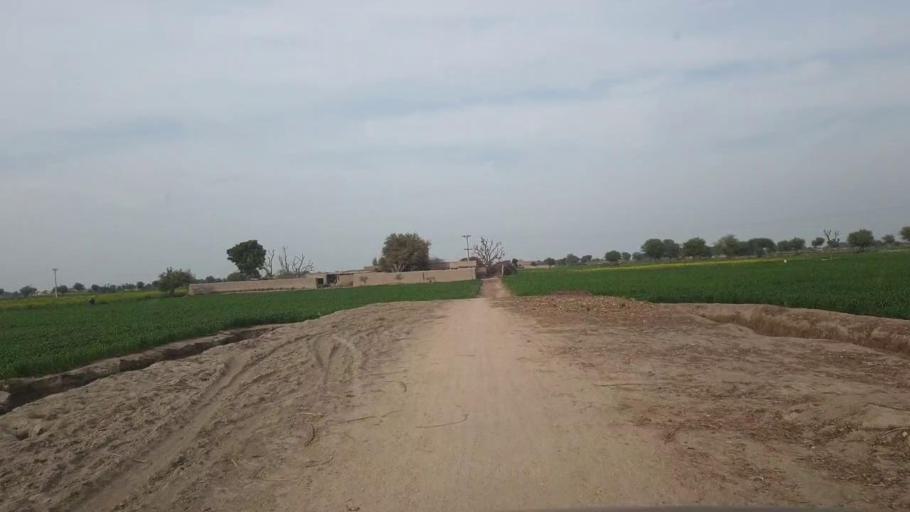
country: PK
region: Sindh
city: Shahpur Chakar
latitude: 26.1208
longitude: 68.5131
